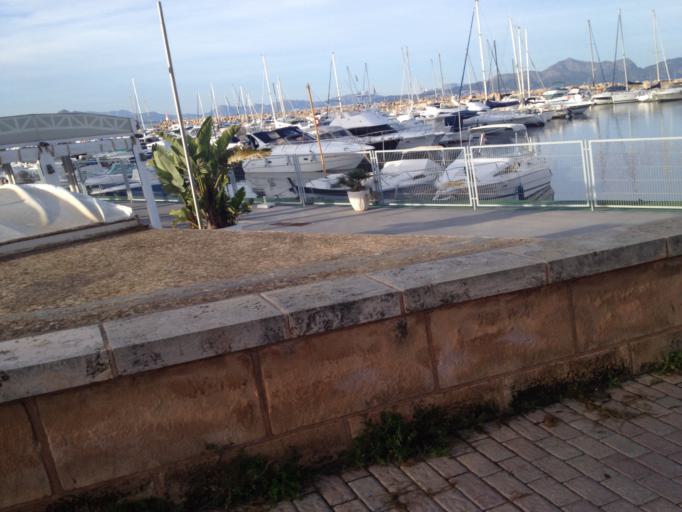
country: ES
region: Balearic Islands
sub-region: Illes Balears
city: Port d'Alcudia
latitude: 39.7649
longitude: 3.1601
